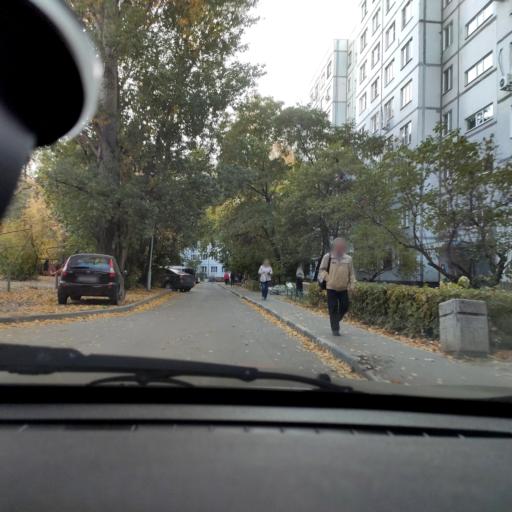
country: RU
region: Samara
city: Tol'yatti
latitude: 53.5322
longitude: 49.2841
